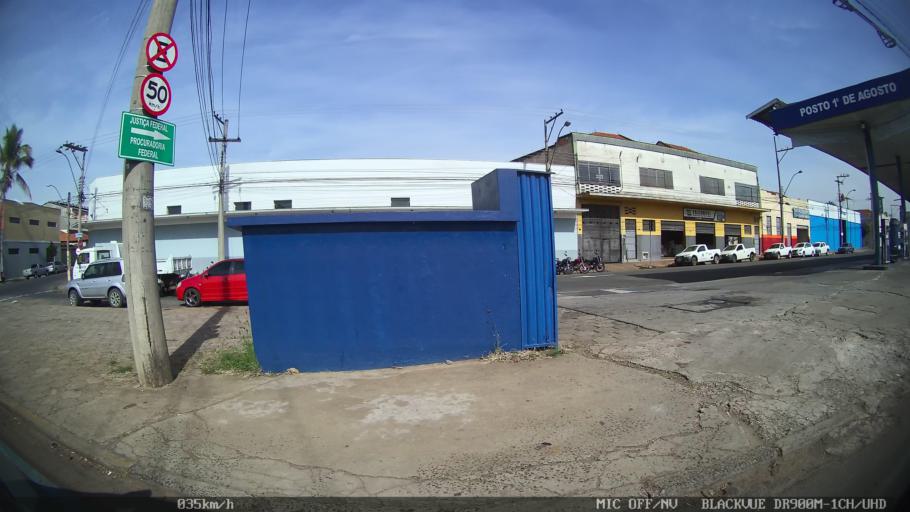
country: BR
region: Sao Paulo
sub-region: Piracicaba
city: Piracicaba
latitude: -22.7058
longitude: -47.6550
